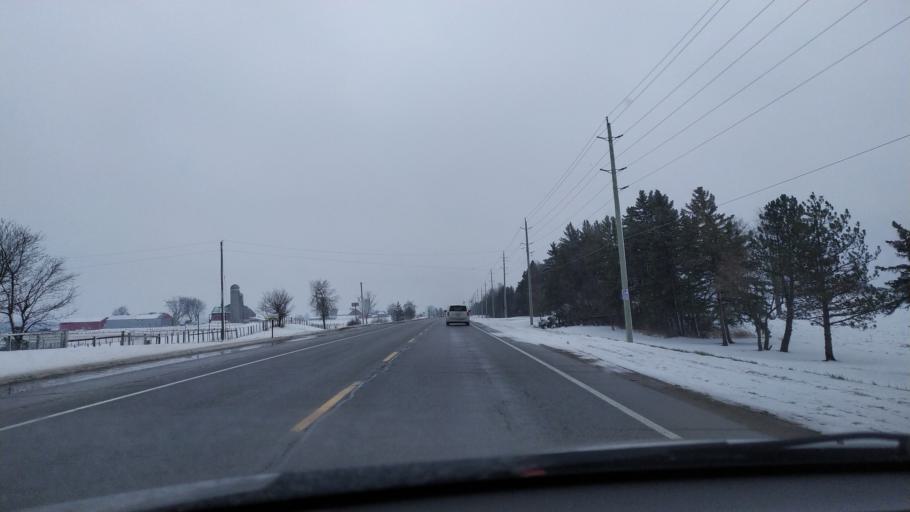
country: CA
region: Ontario
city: Waterloo
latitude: 43.6210
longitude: -80.6881
